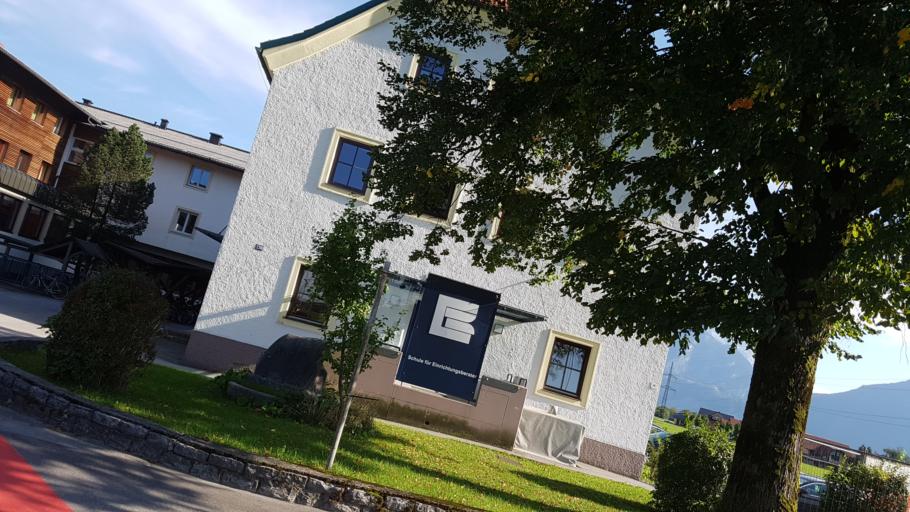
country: AT
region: Salzburg
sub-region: Politischer Bezirk Hallein
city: Kuchl
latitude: 47.6318
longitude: 13.1494
